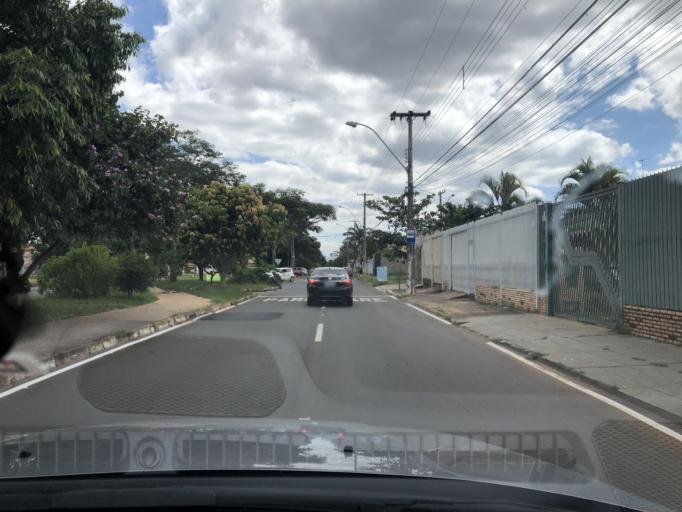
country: BR
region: Federal District
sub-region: Brasilia
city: Brasilia
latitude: -15.9940
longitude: -47.9945
